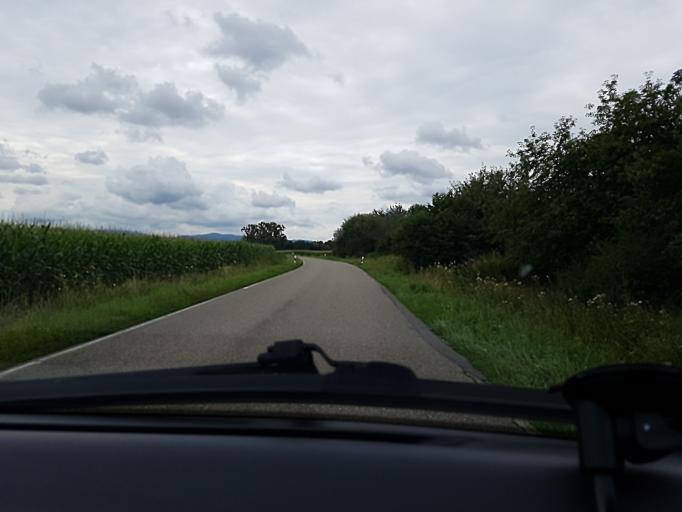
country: DE
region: Baden-Wuerttemberg
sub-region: Freiburg Region
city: Willstatt
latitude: 48.5864
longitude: 7.9091
